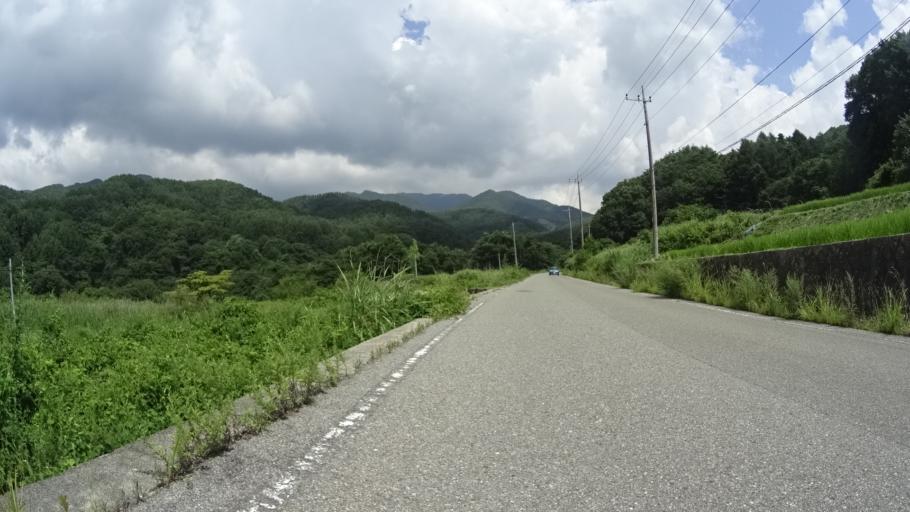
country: JP
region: Yamanashi
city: Nirasaki
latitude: 35.8801
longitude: 138.5199
